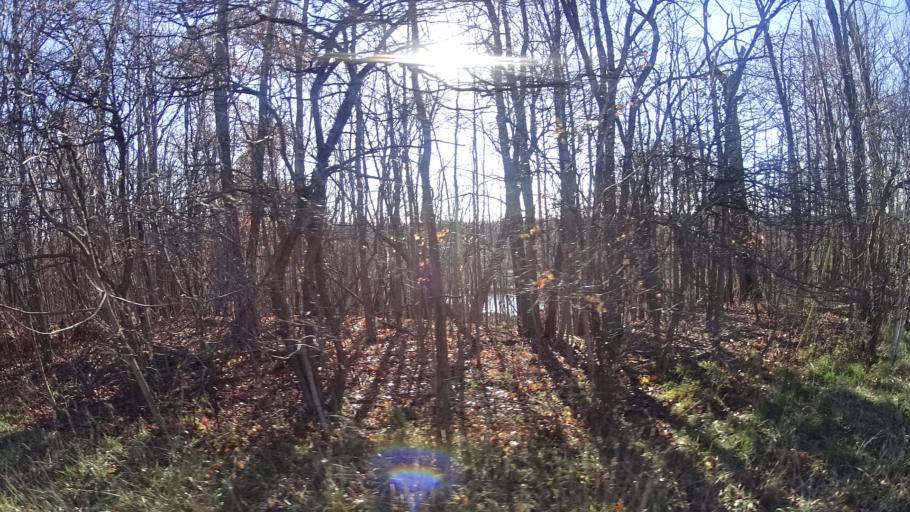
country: US
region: Ohio
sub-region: Lorain County
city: Sheffield
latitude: 41.3989
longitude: -82.1010
